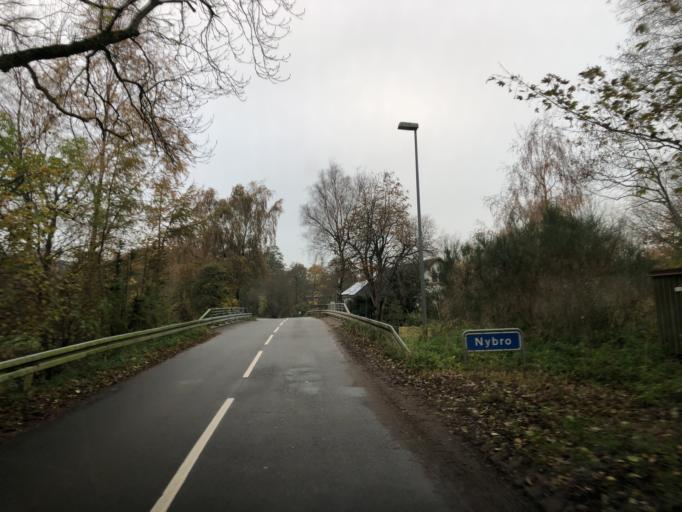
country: DK
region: Central Jutland
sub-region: Herning Kommune
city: Avlum
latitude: 56.2469
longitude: 8.8819
